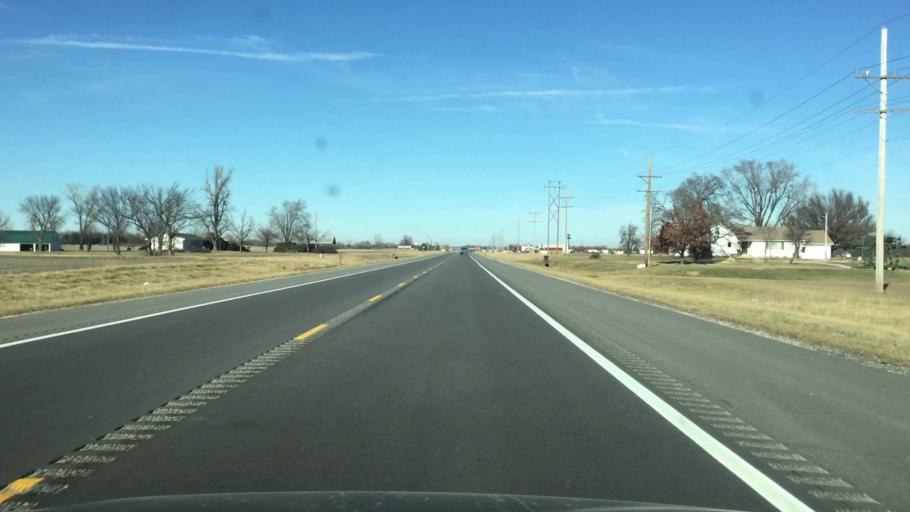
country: US
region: Kansas
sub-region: Franklin County
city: Ottawa
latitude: 38.5590
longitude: -95.2679
